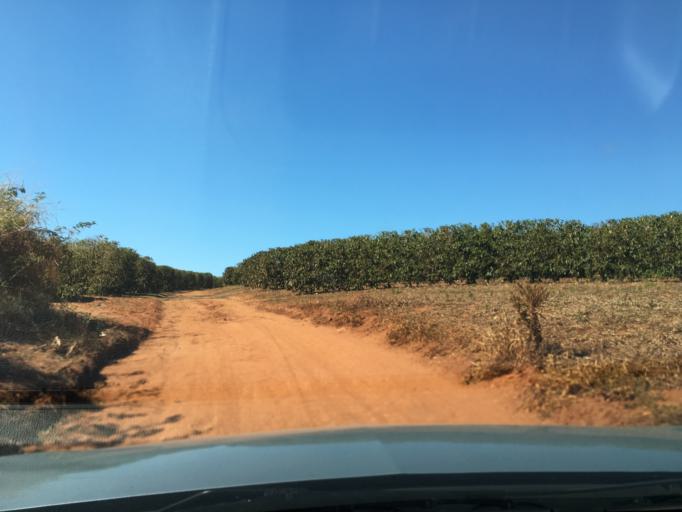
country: BR
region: Minas Gerais
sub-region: Campestre
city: Campestre
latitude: -21.5841
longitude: -46.2071
